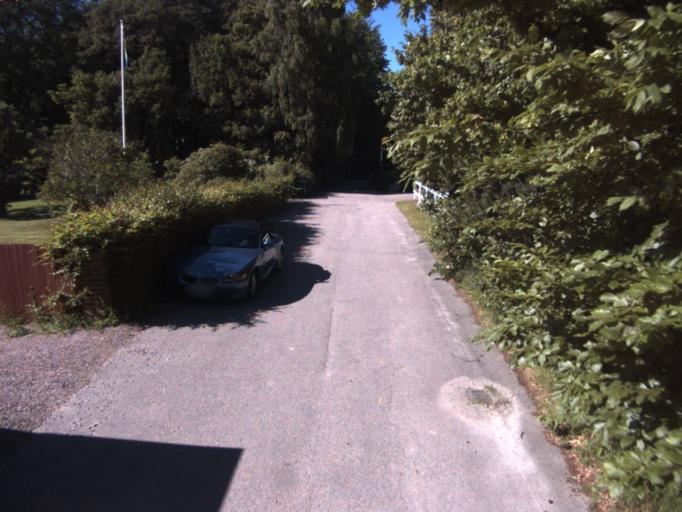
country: SE
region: Skane
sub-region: Helsingborg
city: Odakra
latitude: 56.0988
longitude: 12.7349
